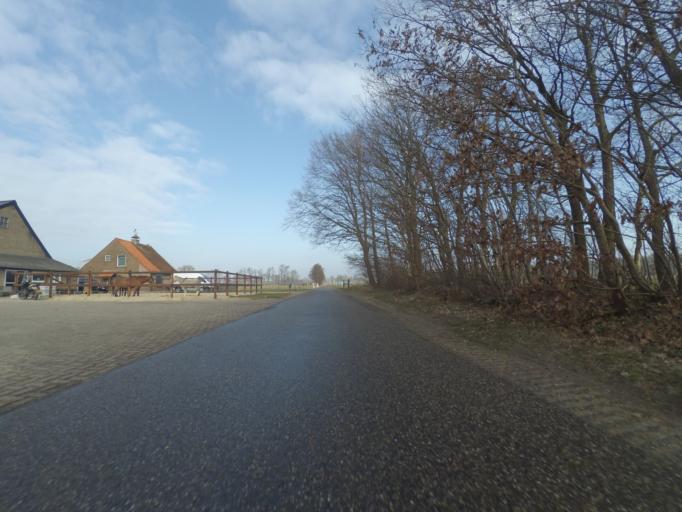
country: NL
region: Utrecht
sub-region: Gemeente Utrechtse Heuvelrug
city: Overberg
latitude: 52.0415
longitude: 5.4602
